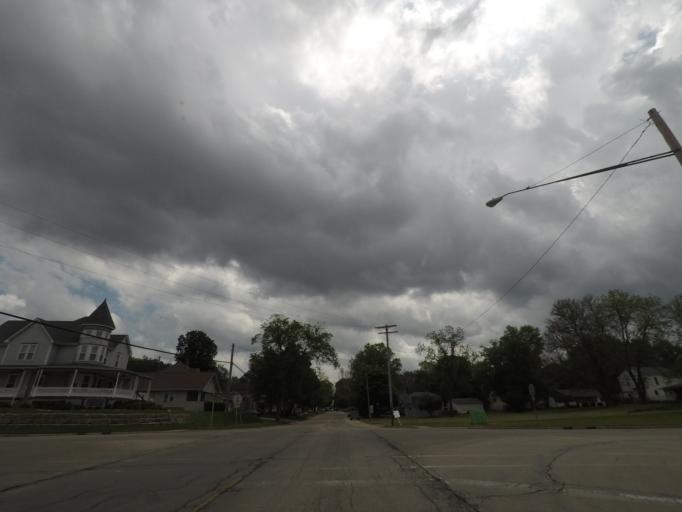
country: US
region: Illinois
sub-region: De Witt County
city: Clinton
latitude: 40.1601
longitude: -88.9606
